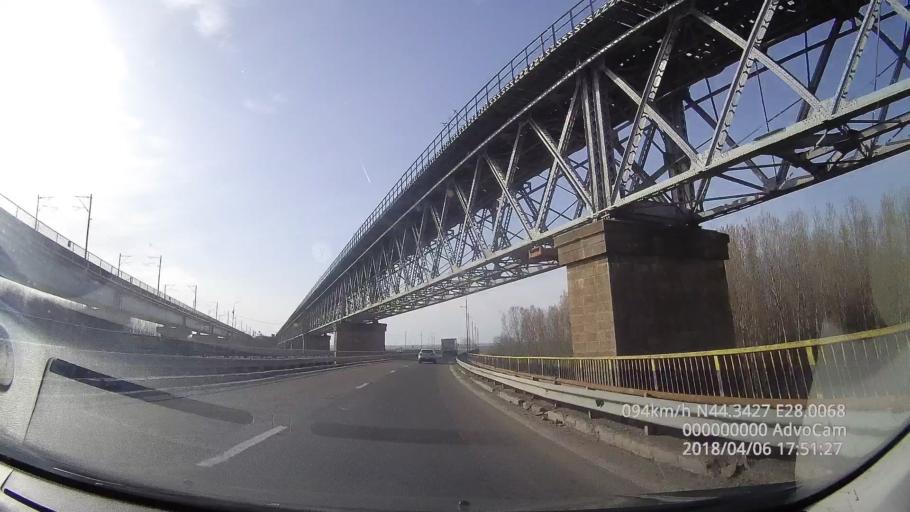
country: RO
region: Constanta
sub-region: Oras Cernavoda
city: Cernavoda
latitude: 44.3430
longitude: 28.0062
